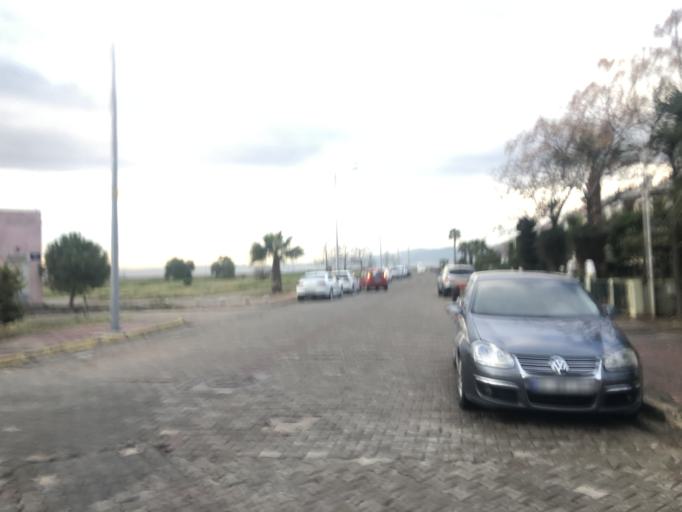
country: TR
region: Izmir
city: Karsiyaka
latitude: 38.4678
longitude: 27.0680
